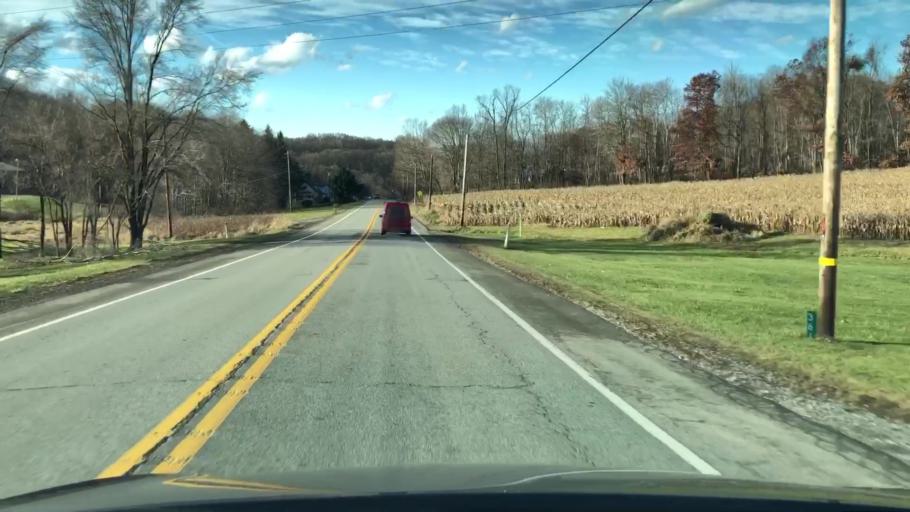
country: US
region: Pennsylvania
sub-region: Butler County
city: Meadowood
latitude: 40.8207
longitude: -79.8526
